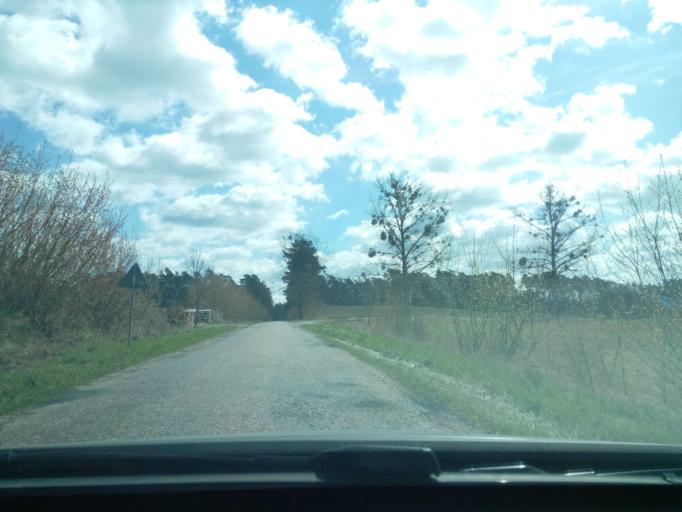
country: PL
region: Warmian-Masurian Voivodeship
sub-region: Powiat nowomiejski
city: Biskupiec
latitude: 53.4572
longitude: 19.2817
